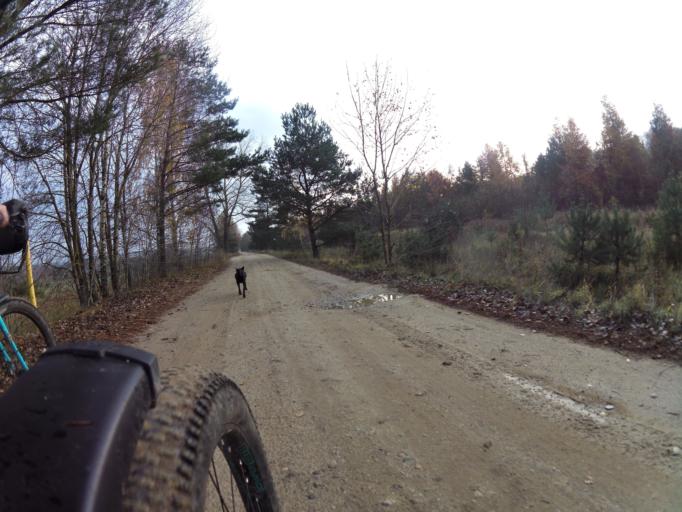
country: PL
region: Pomeranian Voivodeship
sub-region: Powiat wejherowski
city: Gniewino
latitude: 54.7039
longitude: 18.1058
